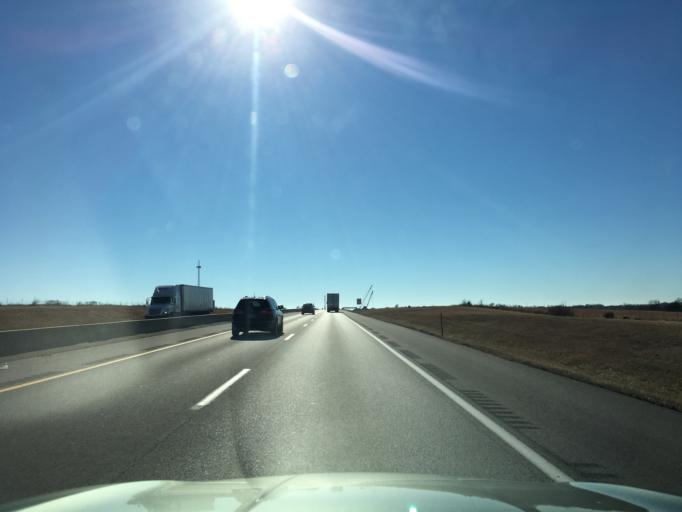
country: US
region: Kansas
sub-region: Sumner County
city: Wellington
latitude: 37.2536
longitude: -97.3390
